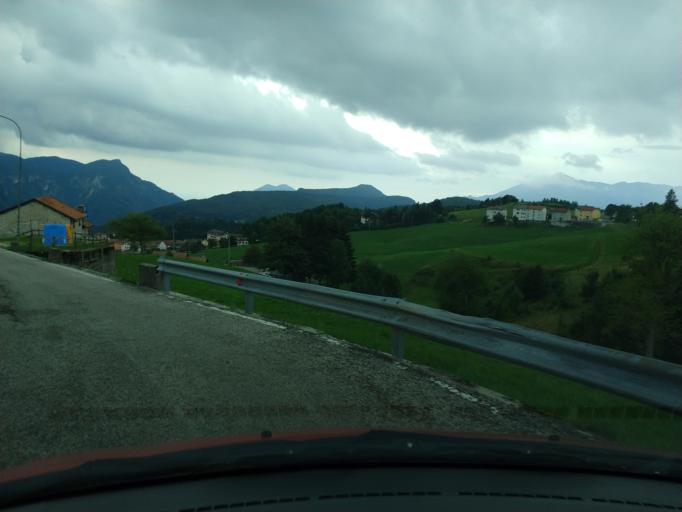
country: IT
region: Veneto
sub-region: Provincia di Vicenza
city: Tonezza del Cimone
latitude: 45.8652
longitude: 11.3360
